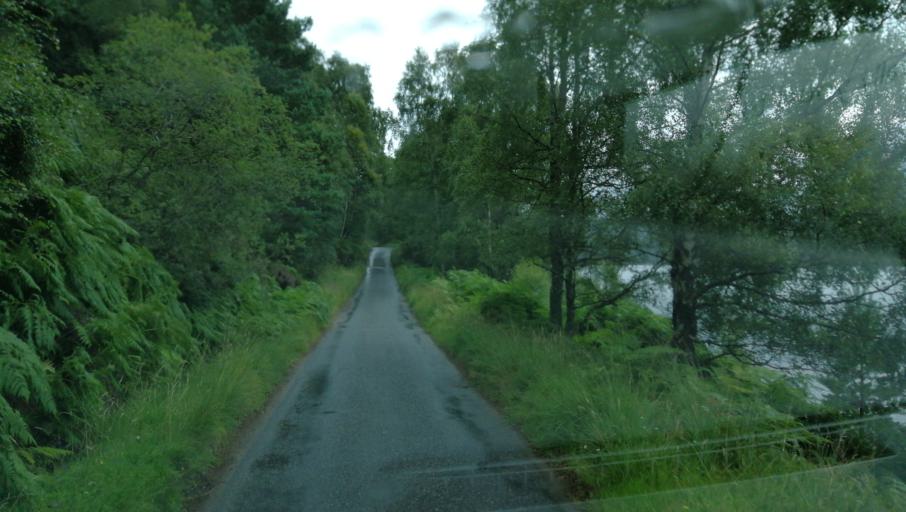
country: GB
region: Scotland
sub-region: Highland
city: Spean Bridge
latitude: 57.2749
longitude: -4.9561
